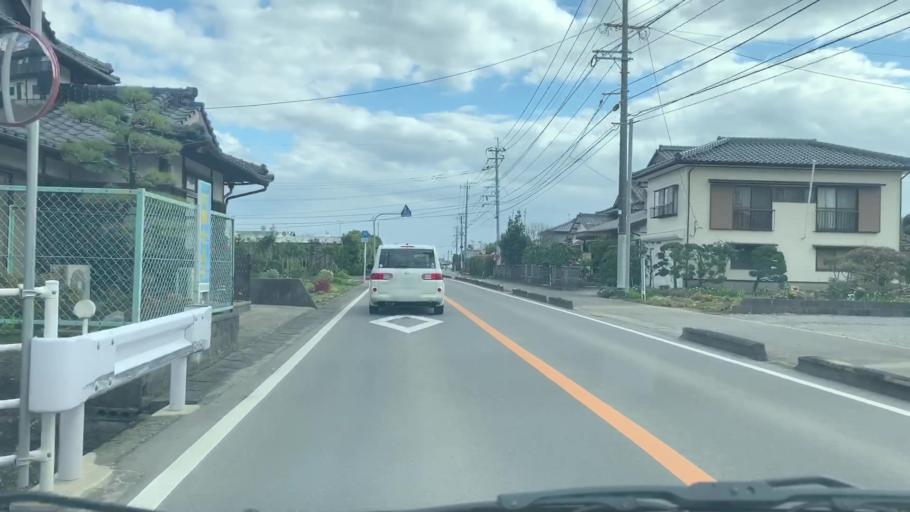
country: JP
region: Saga Prefecture
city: Kashima
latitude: 33.1945
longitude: 130.1148
